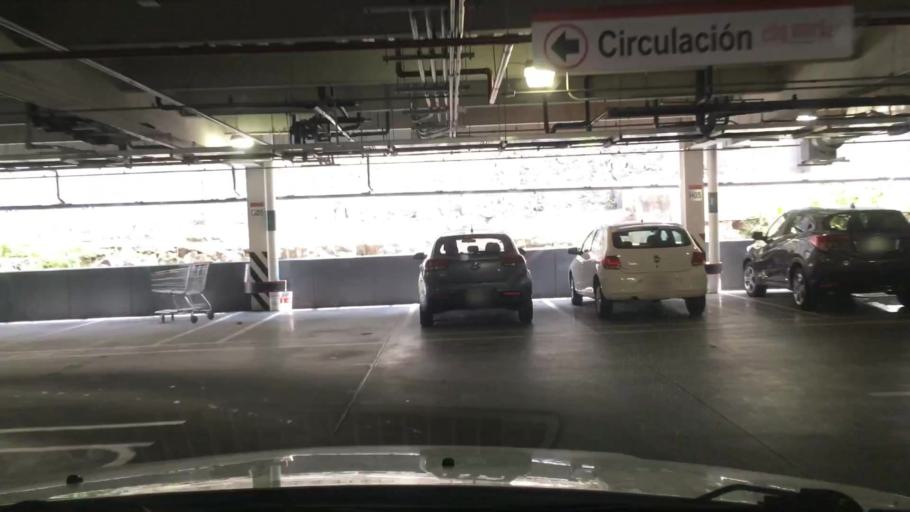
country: MX
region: Mexico City
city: Magdalena Contreras
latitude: 19.3355
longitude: -99.1963
